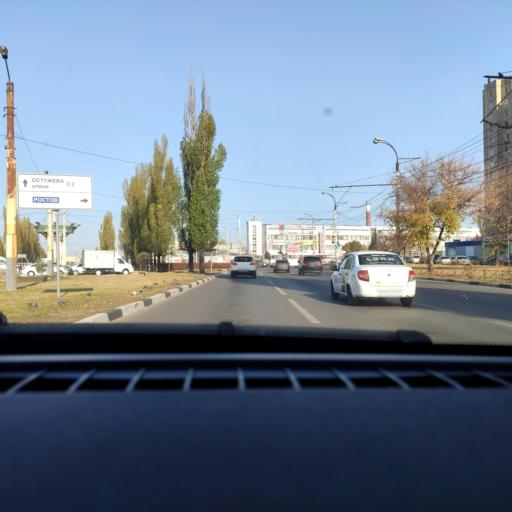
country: RU
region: Voronezj
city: Voronezh
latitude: 51.6843
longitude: 39.2632
